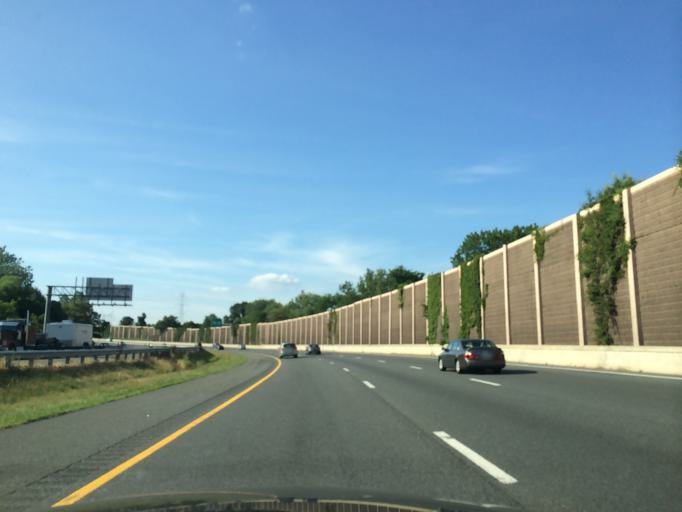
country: US
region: Maryland
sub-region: Howard County
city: Ilchester
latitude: 39.2164
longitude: -76.7951
